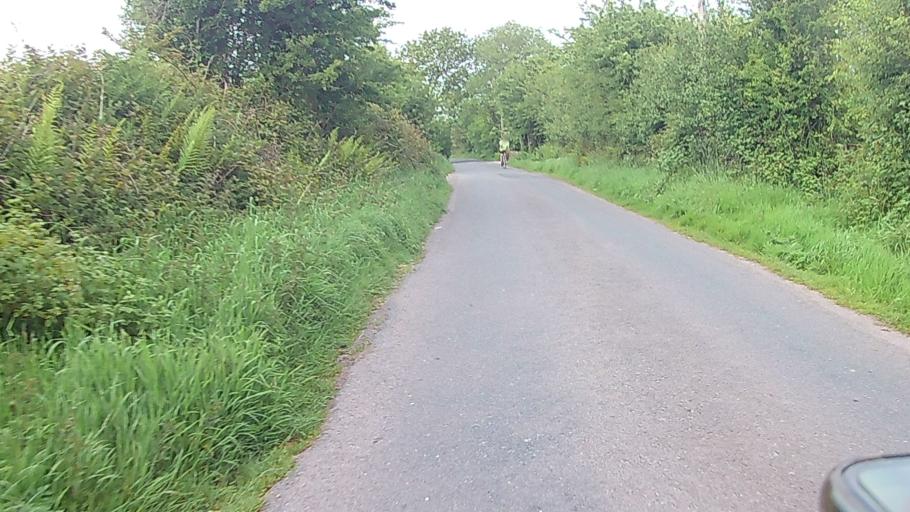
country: IE
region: Munster
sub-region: County Cork
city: Watergrasshill
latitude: 51.9853
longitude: -8.4043
